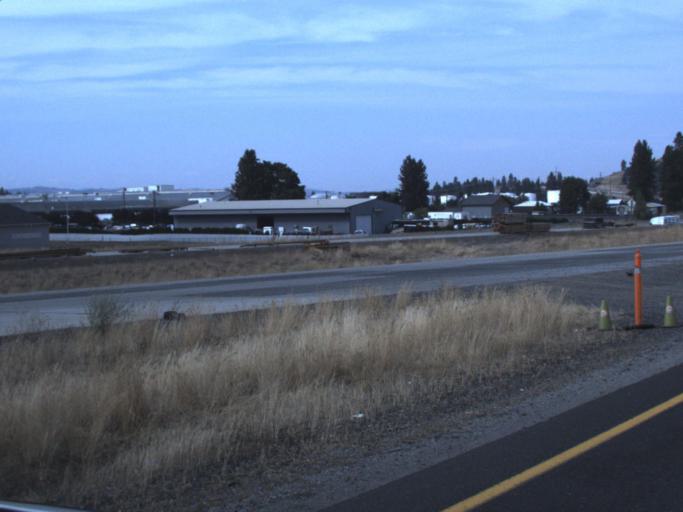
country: US
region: Washington
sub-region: Spokane County
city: Mead
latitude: 47.7744
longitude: -117.3736
